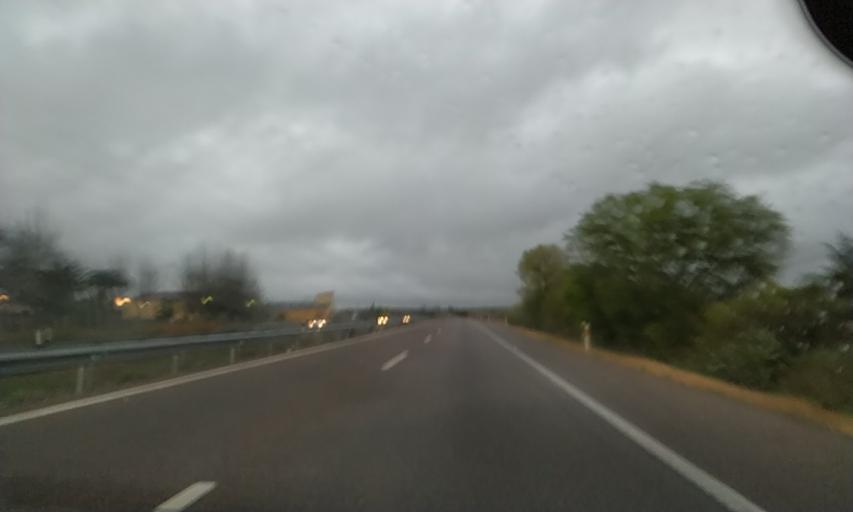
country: ES
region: Extremadura
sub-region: Provincia de Badajoz
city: Calamonte
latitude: 38.8946
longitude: -6.4183
